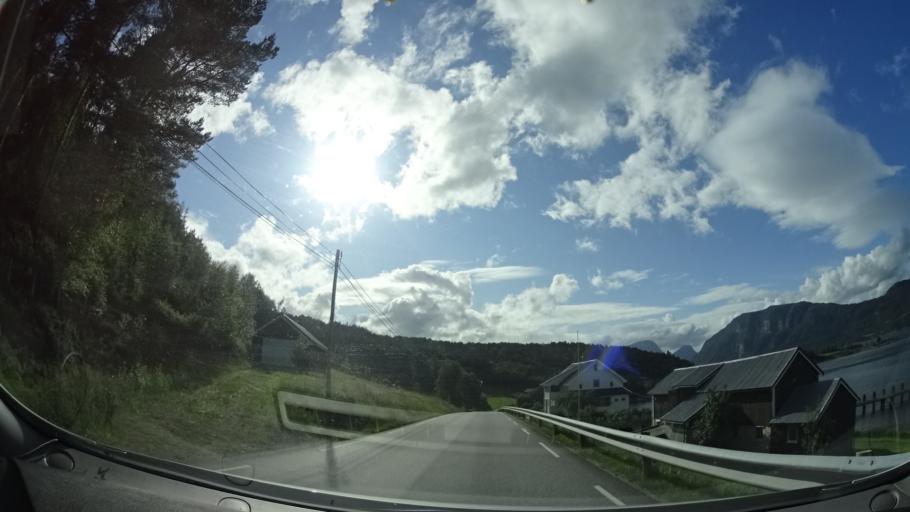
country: NO
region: More og Romsdal
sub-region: Halsa
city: Liaboen
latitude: 63.1357
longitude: 8.4380
